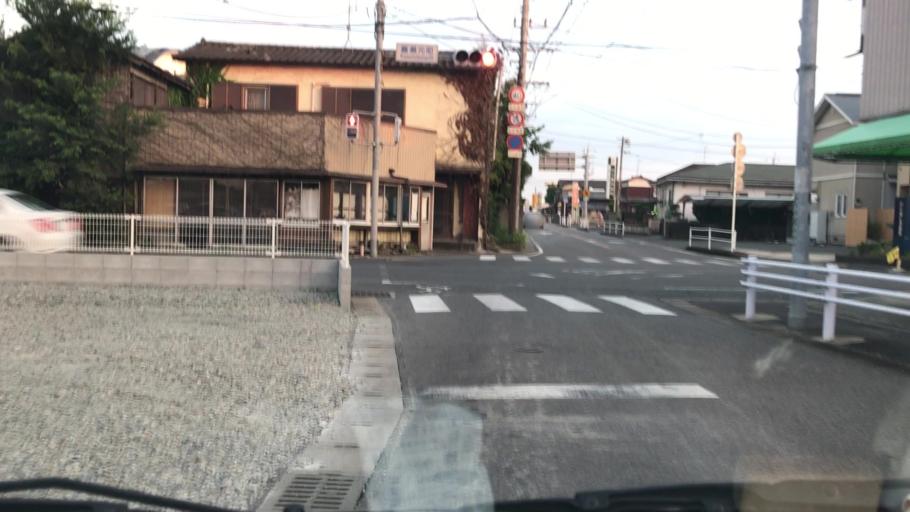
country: JP
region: Saga Prefecture
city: Saga-shi
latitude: 33.2433
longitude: 130.2580
